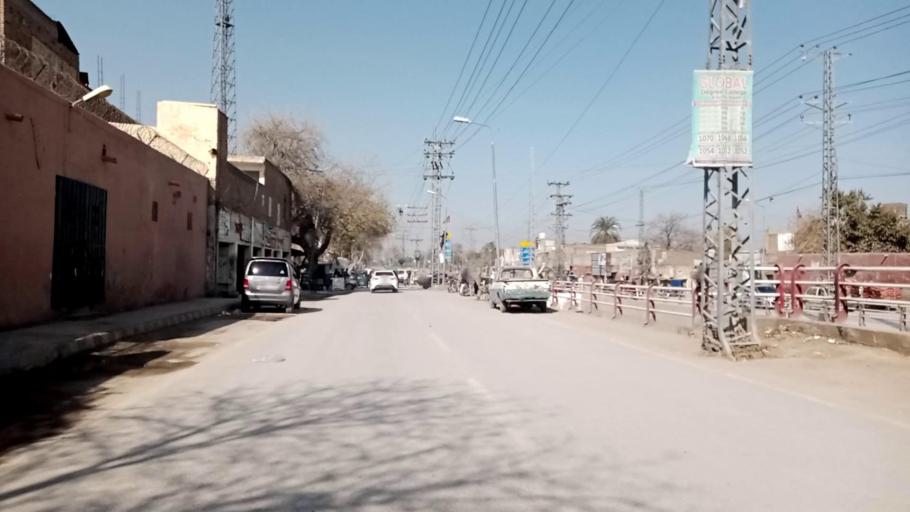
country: PK
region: Khyber Pakhtunkhwa
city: Peshawar
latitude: 33.9905
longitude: 71.4863
